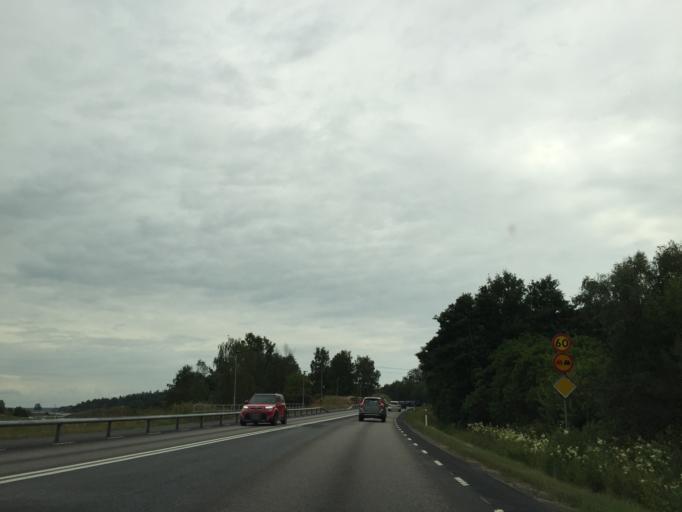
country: SE
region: Vaestra Goetaland
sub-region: Tjorns Kommun
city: Myggenas
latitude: 58.0563
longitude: 11.7594
